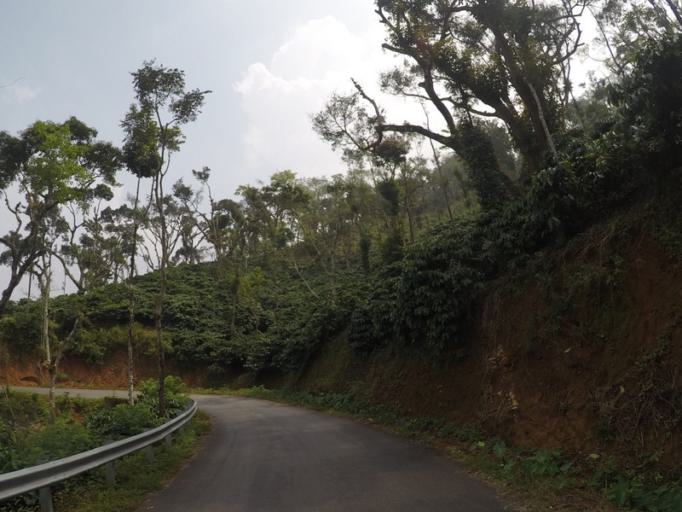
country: IN
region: Karnataka
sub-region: Chikmagalur
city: Mudigere
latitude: 13.1654
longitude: 75.4501
